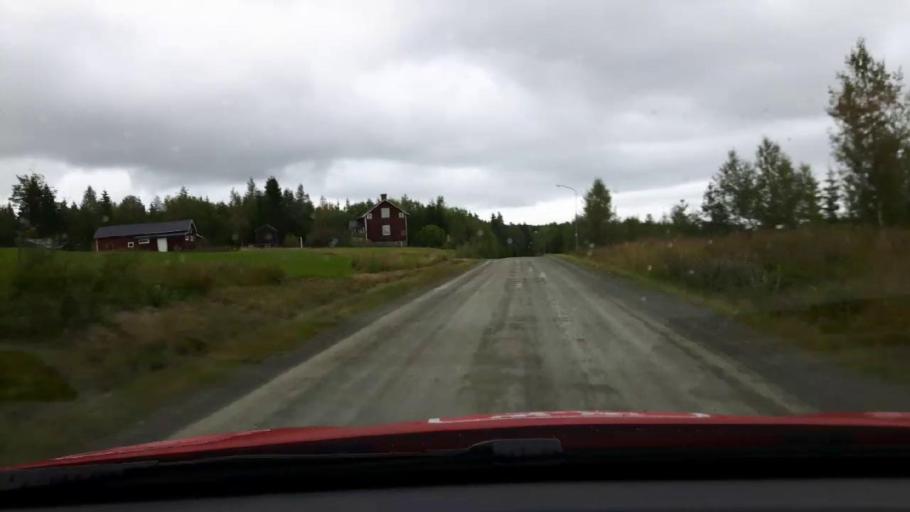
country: SE
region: Jaemtland
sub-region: Bergs Kommun
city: Hoverberg
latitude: 62.8707
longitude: 14.3003
